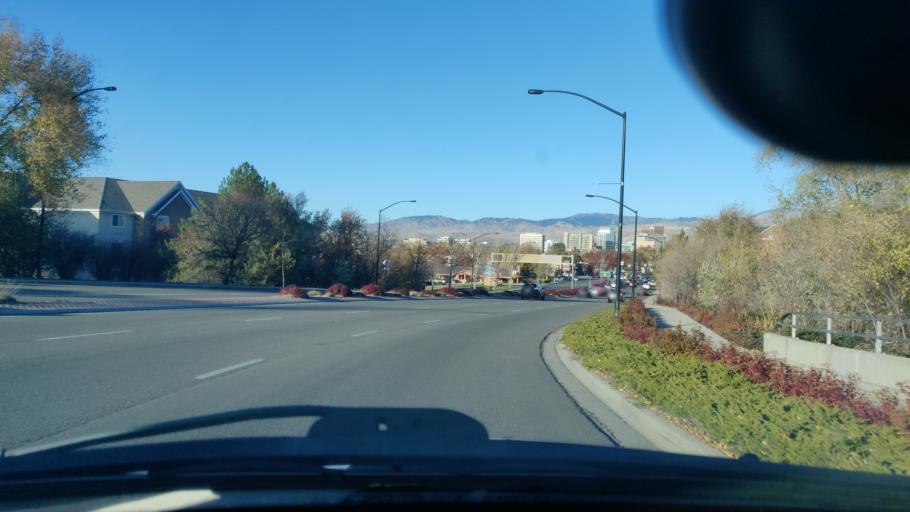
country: US
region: Idaho
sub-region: Ada County
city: Boise
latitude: 43.6032
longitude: -116.2134
